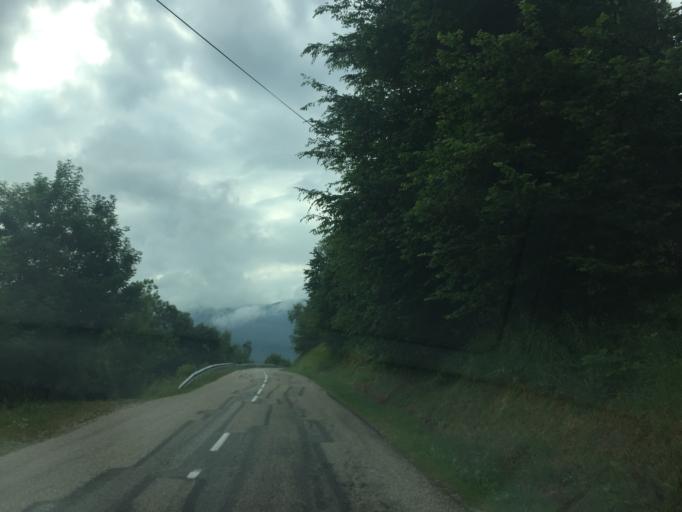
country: FR
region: Rhone-Alpes
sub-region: Departement de la Savoie
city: Barby
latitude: 45.5735
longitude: 6.0041
